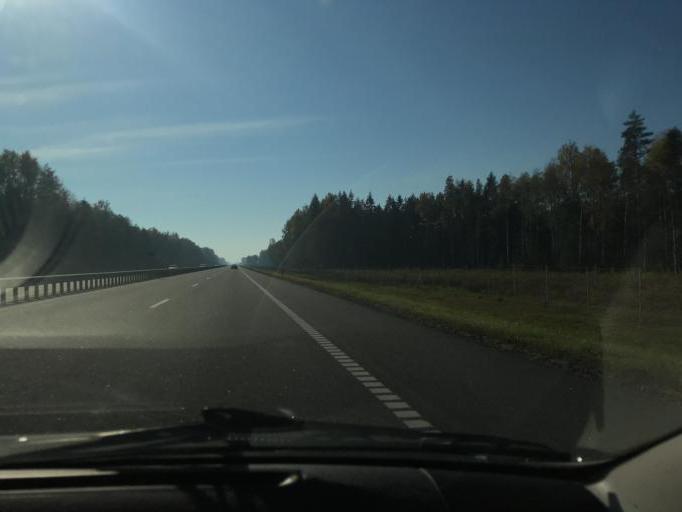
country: BY
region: Minsk
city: Slutsk
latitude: 53.2639
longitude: 27.5501
